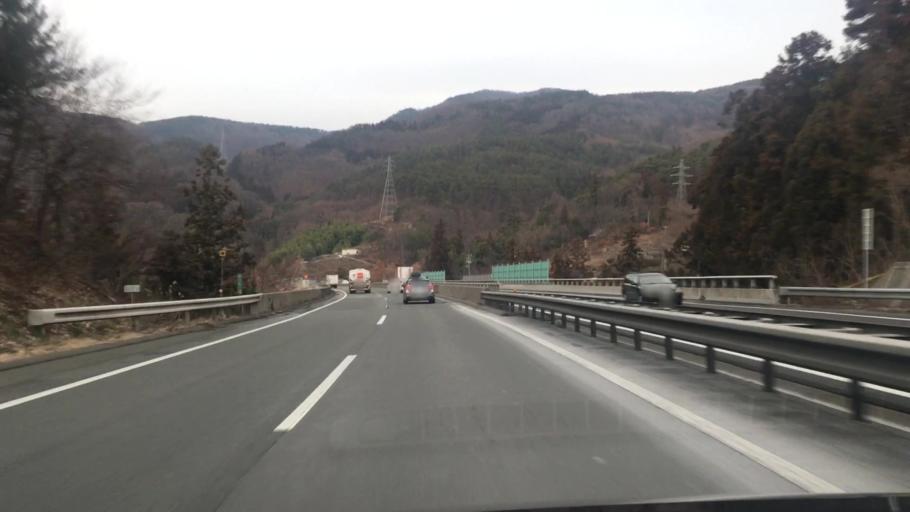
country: JP
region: Nagano
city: Ueda
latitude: 36.4678
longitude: 138.1984
